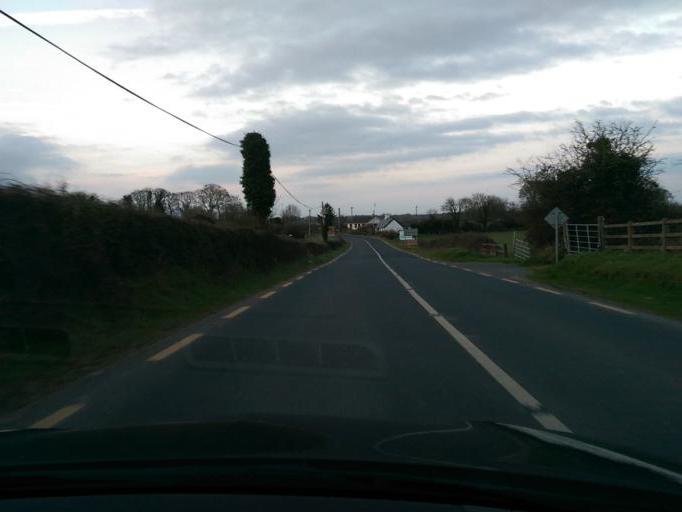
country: IE
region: Connaught
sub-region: County Galway
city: Portumna
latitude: 53.0028
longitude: -8.1261
